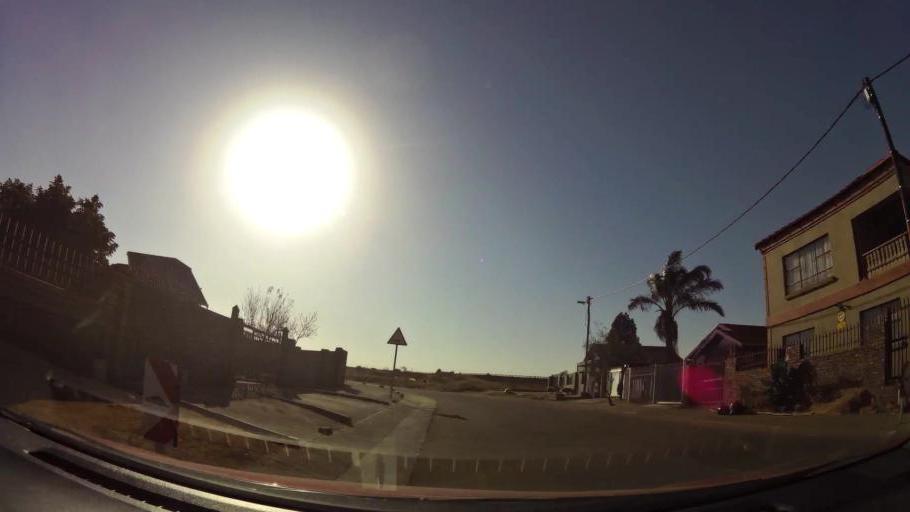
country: ZA
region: Gauteng
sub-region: City of Tshwane Metropolitan Municipality
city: Mabopane
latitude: -25.5834
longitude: 28.1094
